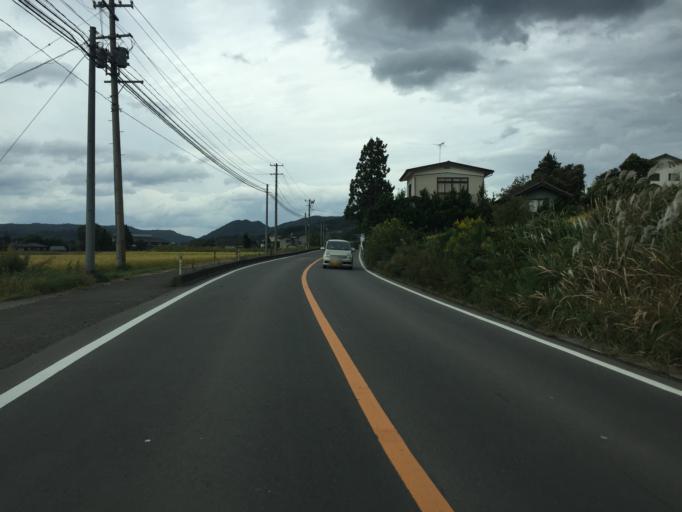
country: JP
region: Fukushima
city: Yanagawamachi-saiwaicho
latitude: 37.8684
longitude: 140.6234
